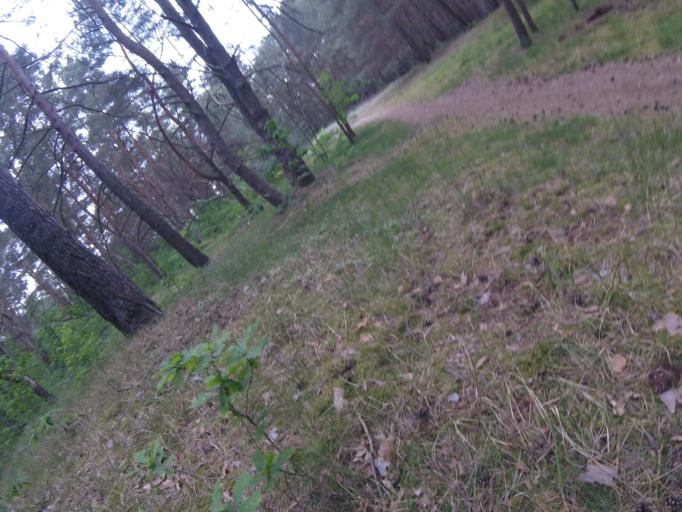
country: DE
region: Brandenburg
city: Bestensee
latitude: 52.2268
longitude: 13.6709
